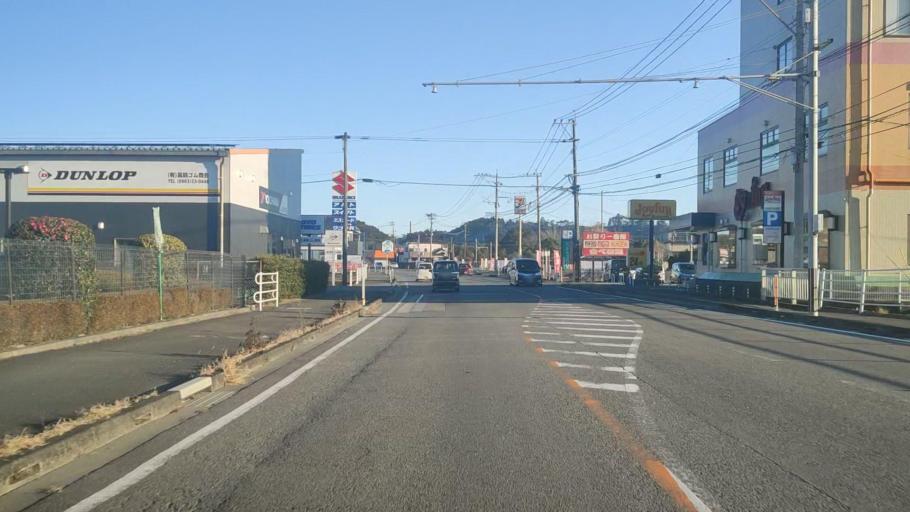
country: JP
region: Miyazaki
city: Takanabe
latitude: 32.1364
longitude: 131.5271
